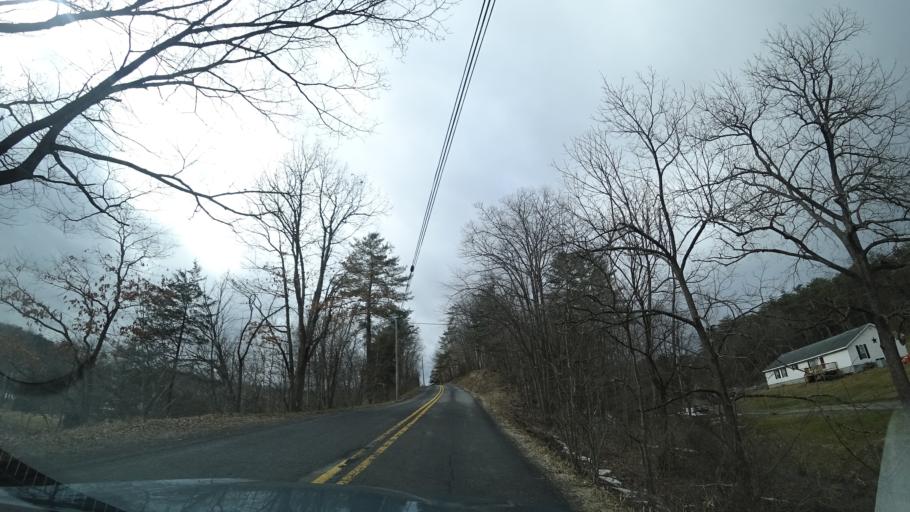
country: US
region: Virginia
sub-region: Shenandoah County
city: Basye
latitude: 38.8773
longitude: -78.8709
